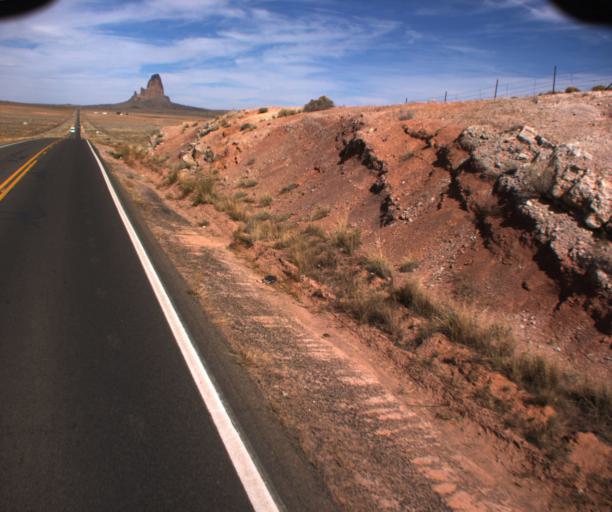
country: US
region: Arizona
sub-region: Navajo County
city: Kayenta
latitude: 36.7563
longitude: -110.2264
